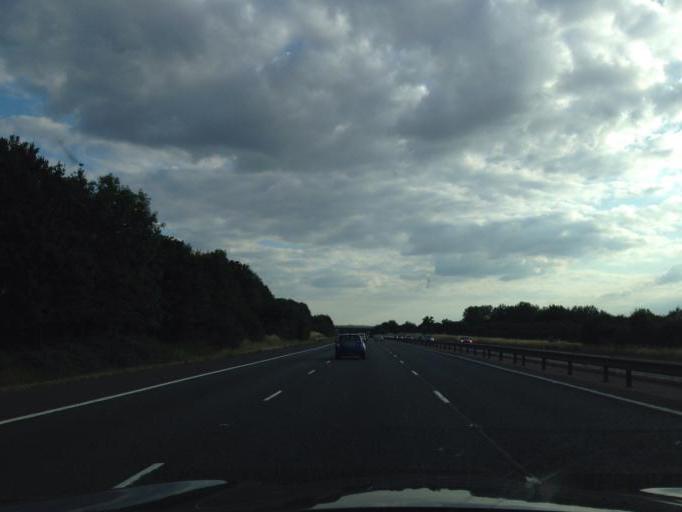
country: GB
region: England
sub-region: Oxfordshire
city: Wheatley
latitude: 51.7859
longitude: -1.0894
